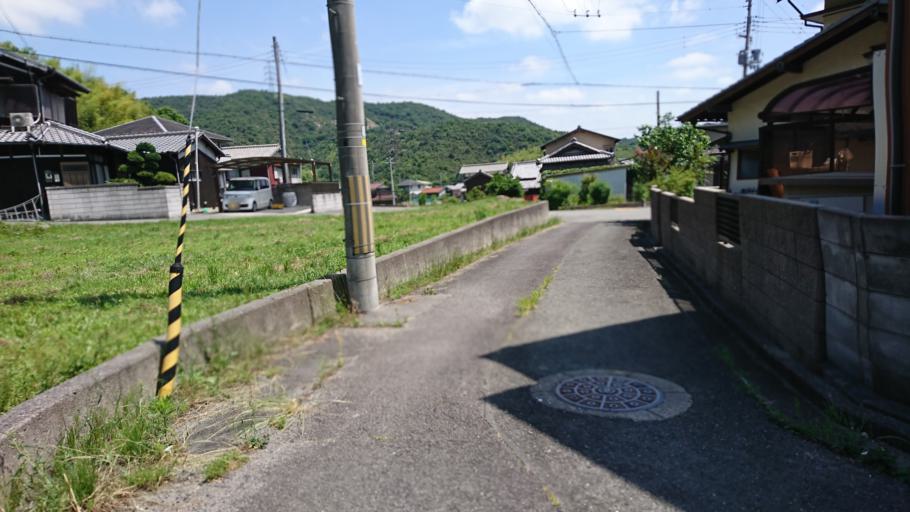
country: JP
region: Hyogo
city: Kakogawacho-honmachi
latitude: 34.8079
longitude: 134.7900
